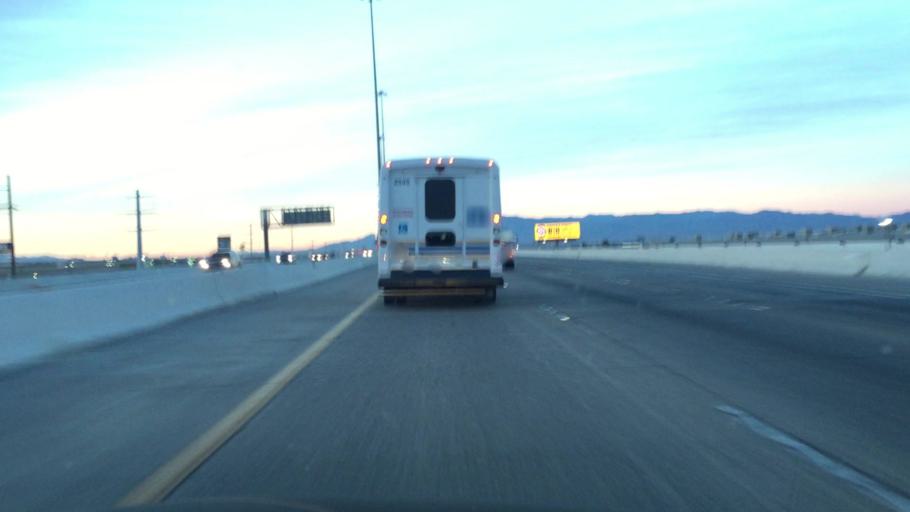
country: US
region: Nevada
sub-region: Clark County
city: Henderson
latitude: 36.0560
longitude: -115.0272
